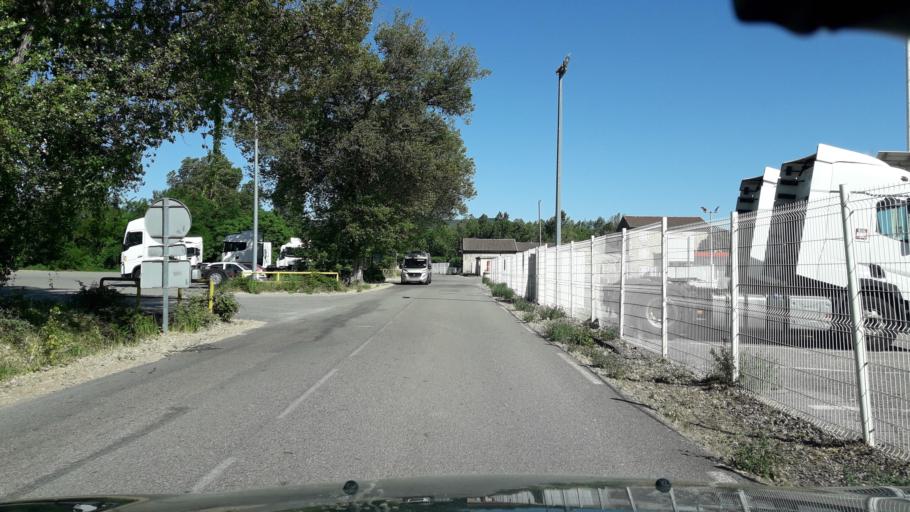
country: FR
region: Rhone-Alpes
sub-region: Departement de la Drome
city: Loriol-sur-Drome
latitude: 44.7481
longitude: 4.7995
